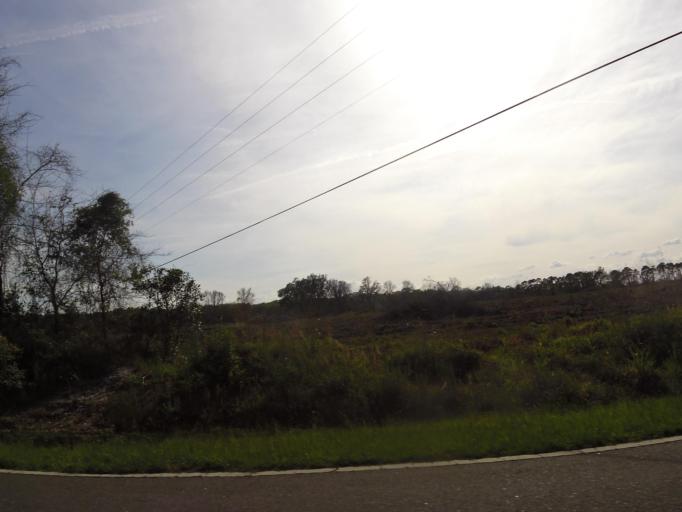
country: US
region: Florida
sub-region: Nassau County
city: Fernandina Beach
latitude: 30.5043
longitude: -81.4739
